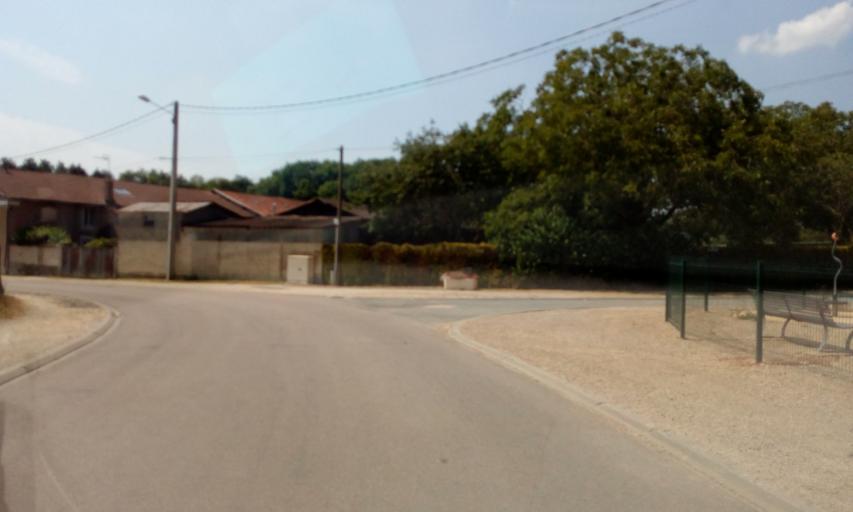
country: FR
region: Lorraine
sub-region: Departement de la Meuse
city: Verdun
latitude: 49.1814
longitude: 5.4976
